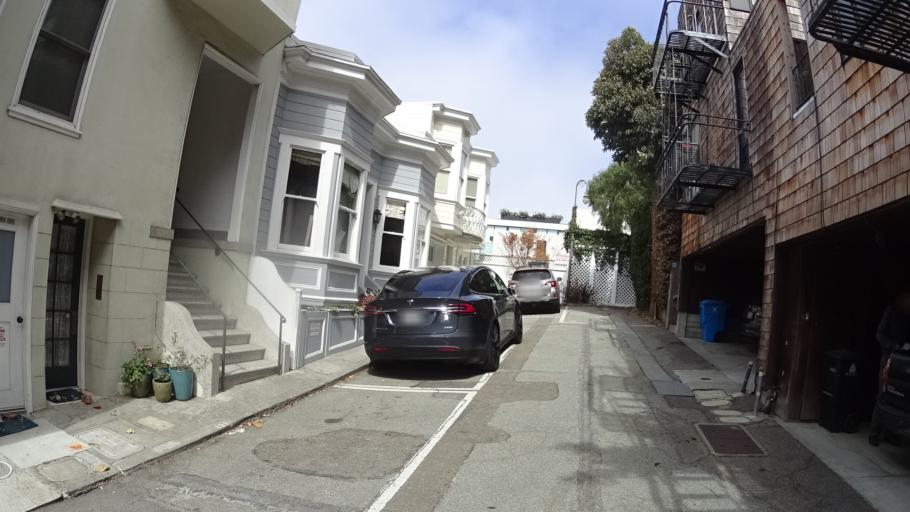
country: US
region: California
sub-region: San Francisco County
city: San Francisco
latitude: 37.8029
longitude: -122.4223
